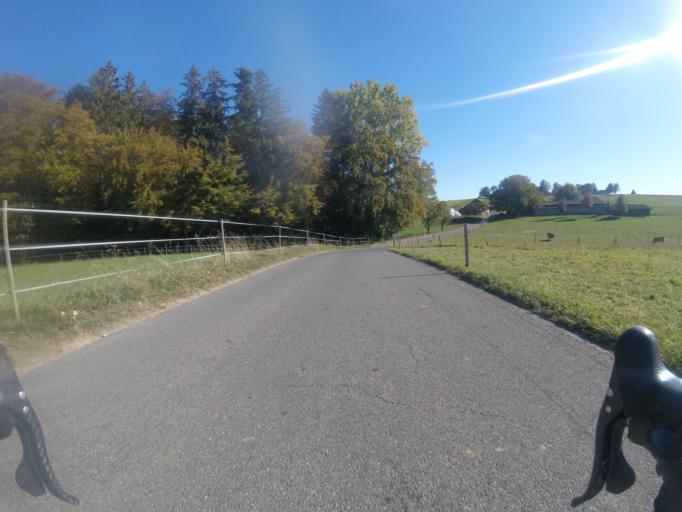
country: CH
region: Bern
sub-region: Seeland District
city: Schupfen
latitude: 47.0278
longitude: 7.3935
